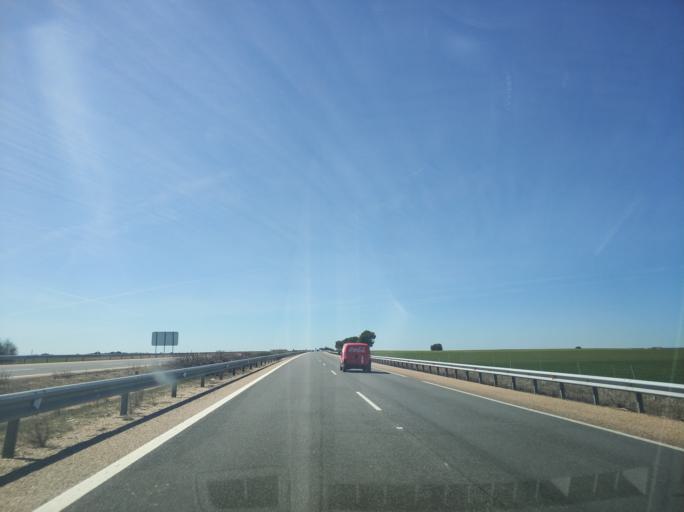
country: ES
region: Castille and Leon
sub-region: Provincia de Salamanca
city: Parada de Rubiales
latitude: 41.1492
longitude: -5.4654
